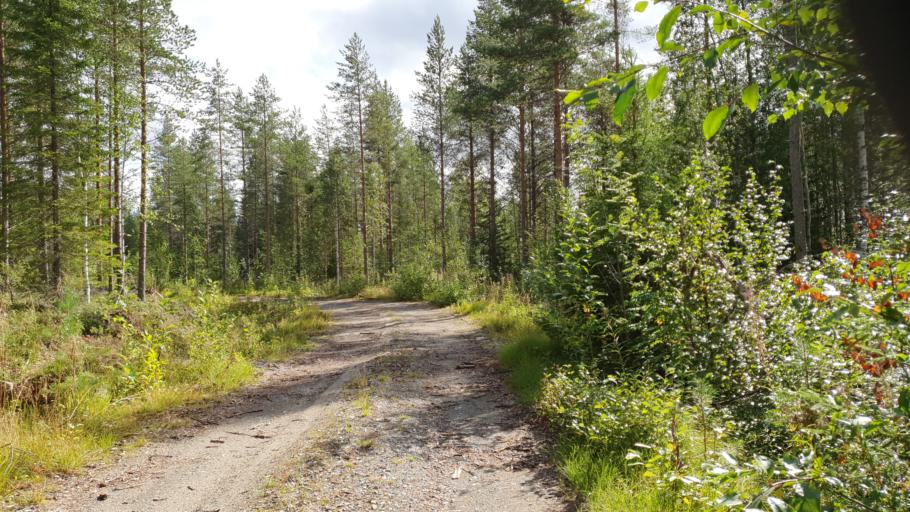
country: FI
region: Kainuu
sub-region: Kehys-Kainuu
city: Kuhmo
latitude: 64.1398
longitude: 29.3890
